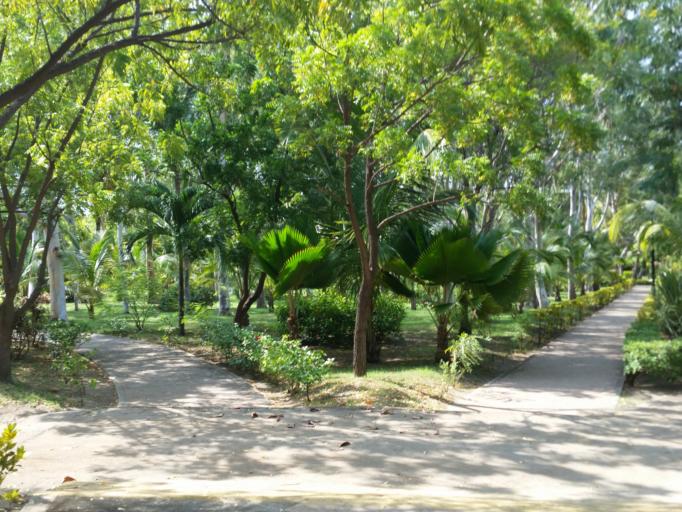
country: NI
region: Managua
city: Masachapa
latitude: 11.8090
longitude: -86.5221
